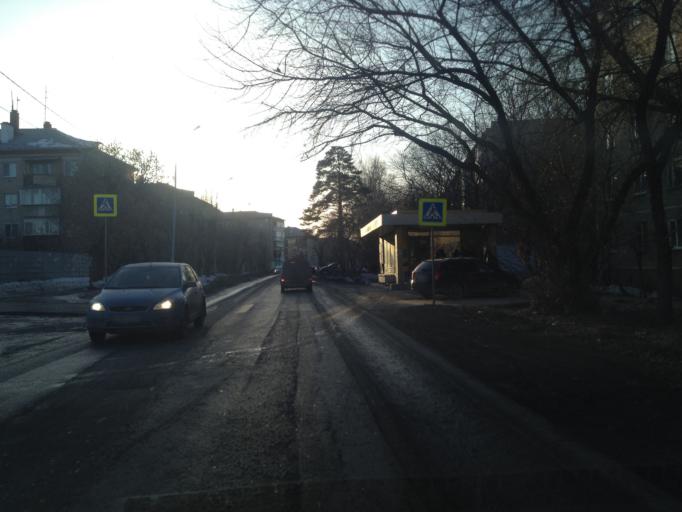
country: RU
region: Sverdlovsk
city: Sovkhoznyy
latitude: 56.7624
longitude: 60.5732
